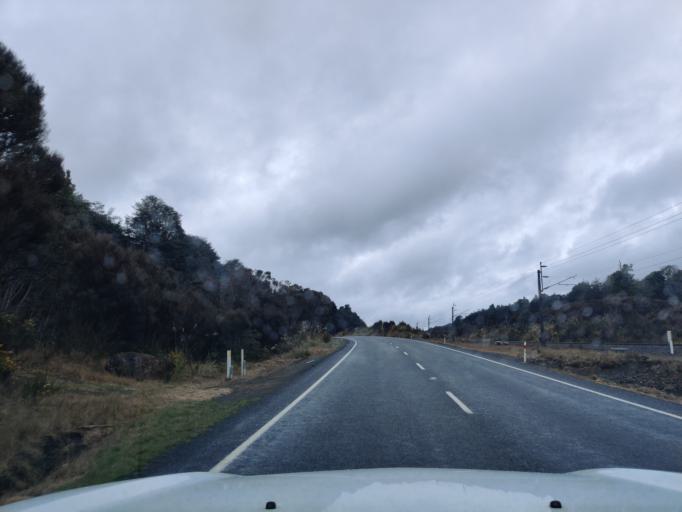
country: NZ
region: Manawatu-Wanganui
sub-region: Ruapehu District
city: Waiouru
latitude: -39.3038
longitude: 175.3898
